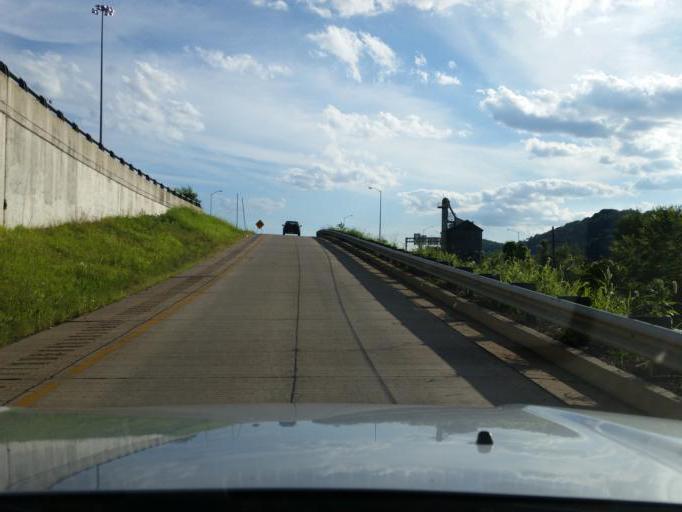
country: US
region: Pennsylvania
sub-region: Allegheny County
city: Etna
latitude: 40.4955
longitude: -79.9414
